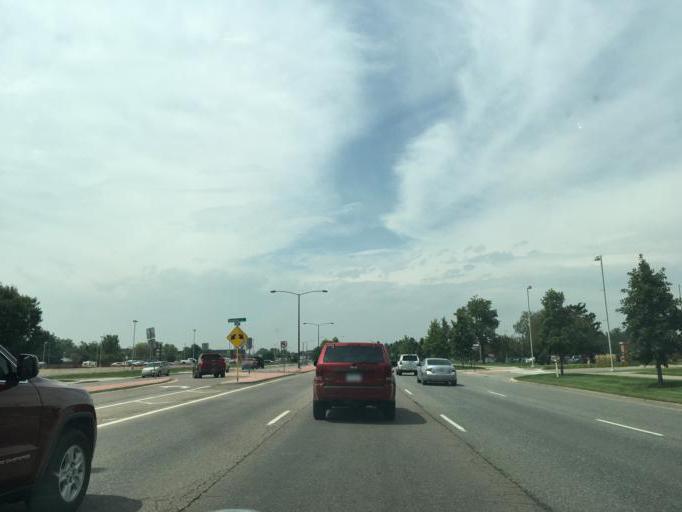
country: US
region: Colorado
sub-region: Adams County
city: Aurora
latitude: 39.7403
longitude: -104.8406
